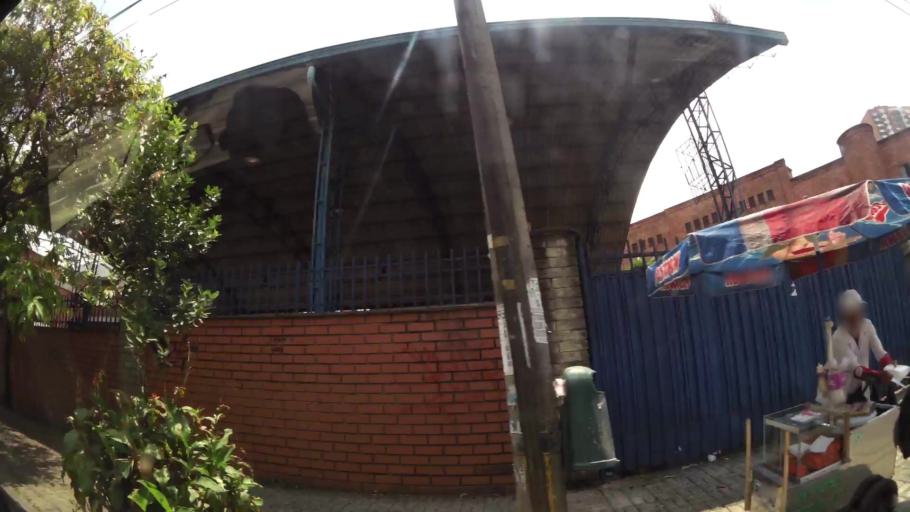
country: CO
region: Antioquia
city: Sabaneta
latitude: 6.1686
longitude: -75.6184
